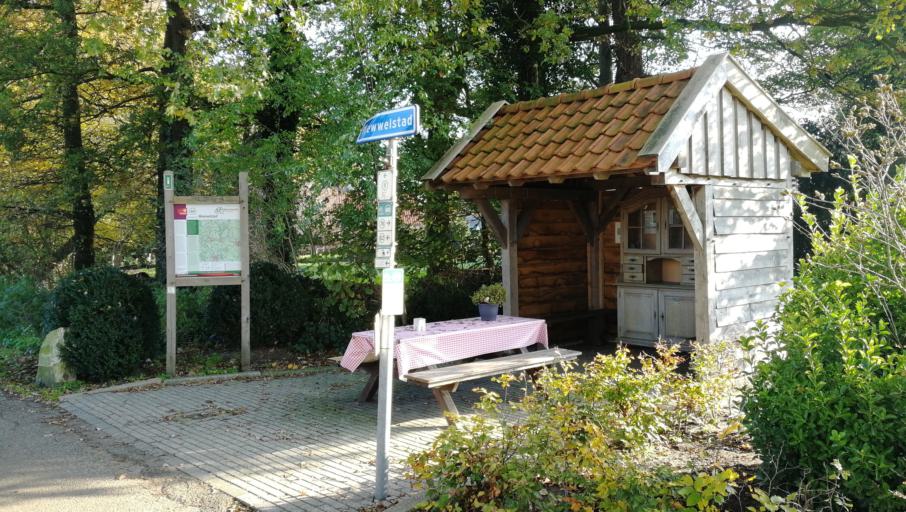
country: NL
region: Overijssel
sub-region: Gemeente Losser
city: Losser
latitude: 52.3074
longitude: 7.0284
